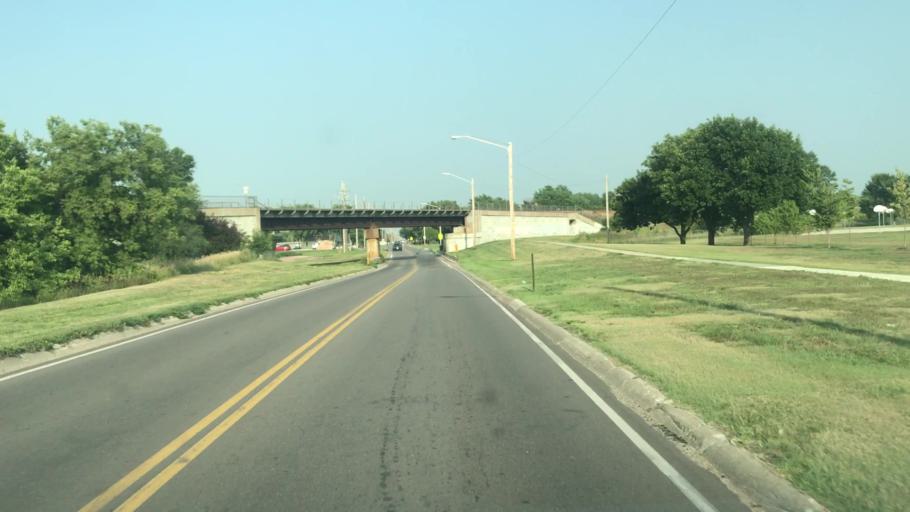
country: US
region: Nebraska
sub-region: Hall County
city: Grand Island
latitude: 40.9457
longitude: -98.3495
